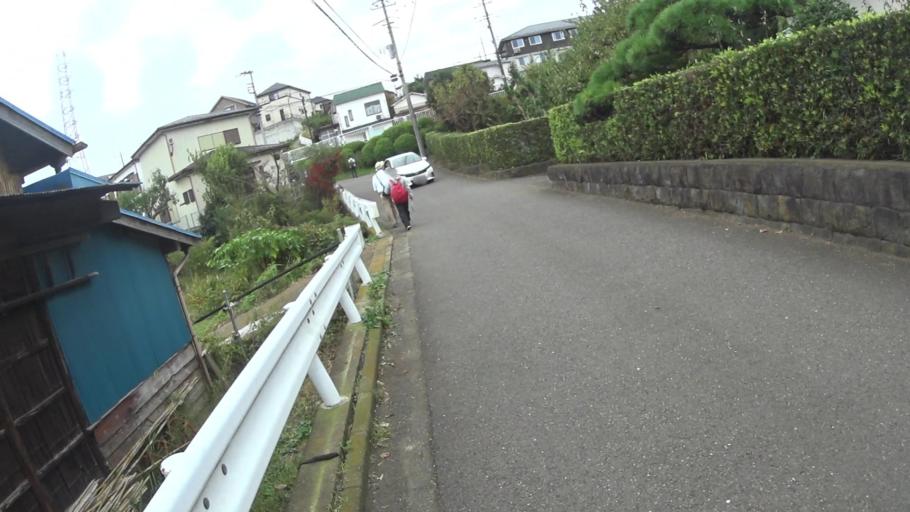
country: JP
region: Kanagawa
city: Hadano
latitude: 35.3882
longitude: 139.2212
